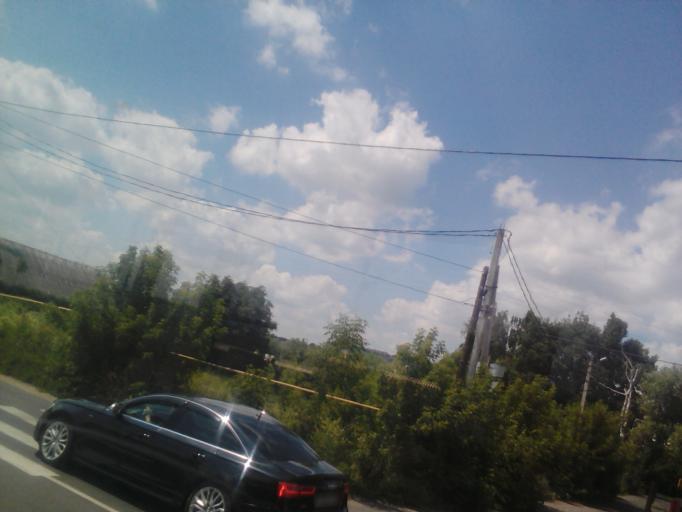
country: RU
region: Kursk
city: Kursk
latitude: 51.7093
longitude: 36.1818
